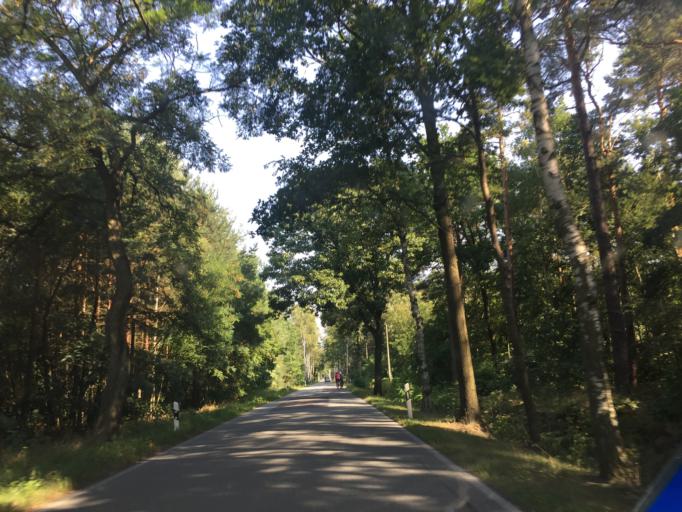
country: DE
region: Saxony
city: Uhyst
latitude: 51.3539
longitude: 14.5067
